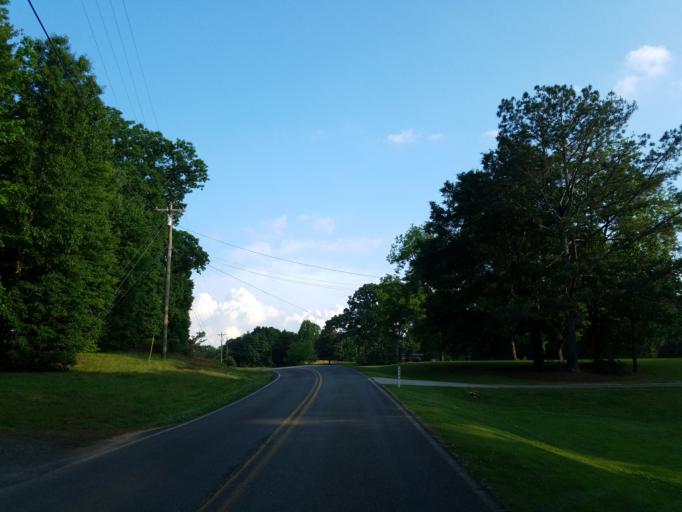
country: US
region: Georgia
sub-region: Cherokee County
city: Ball Ground
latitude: 34.3271
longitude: -84.3682
